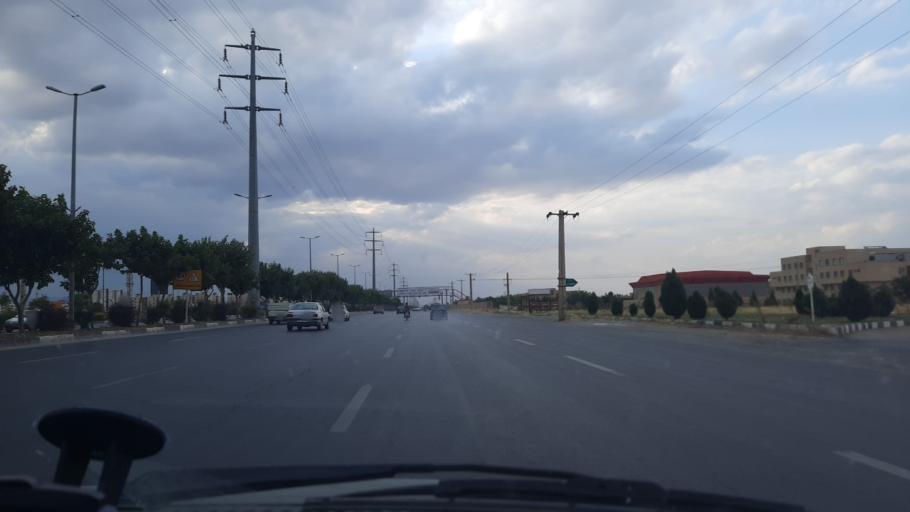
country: IR
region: Markazi
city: Arak
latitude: 34.0985
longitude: 49.7529
